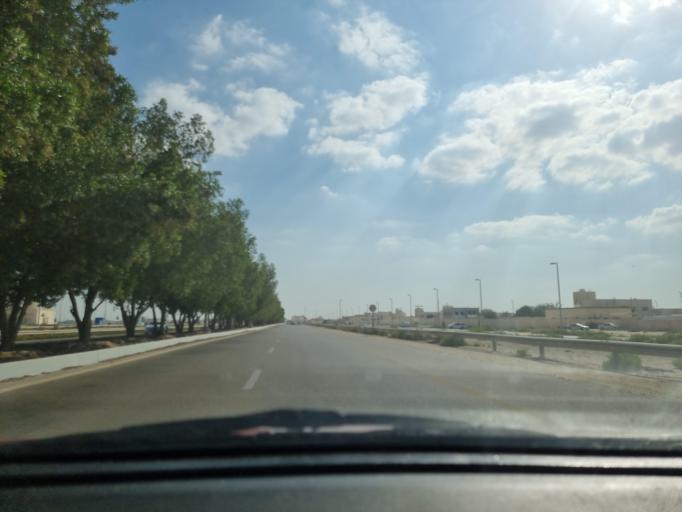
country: AE
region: Abu Dhabi
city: Abu Dhabi
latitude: 24.3855
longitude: 54.7052
